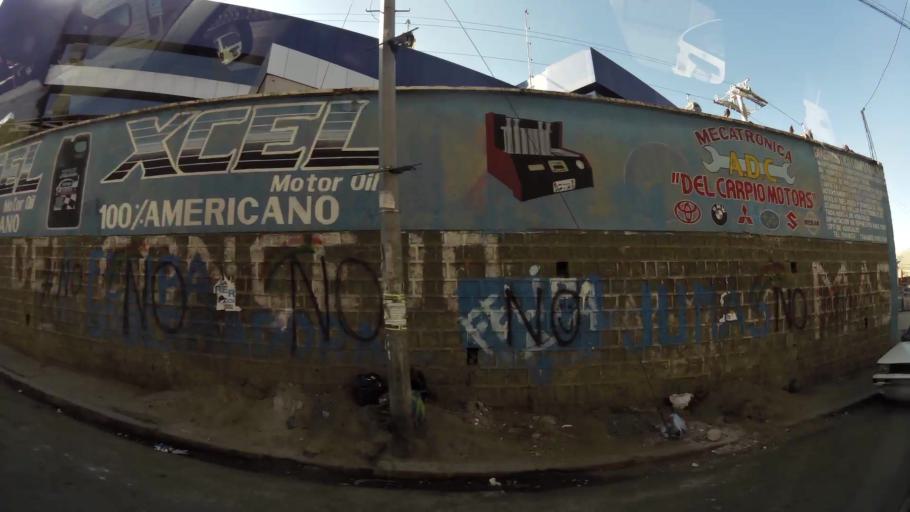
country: BO
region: La Paz
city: La Paz
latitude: -16.5156
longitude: -68.1386
